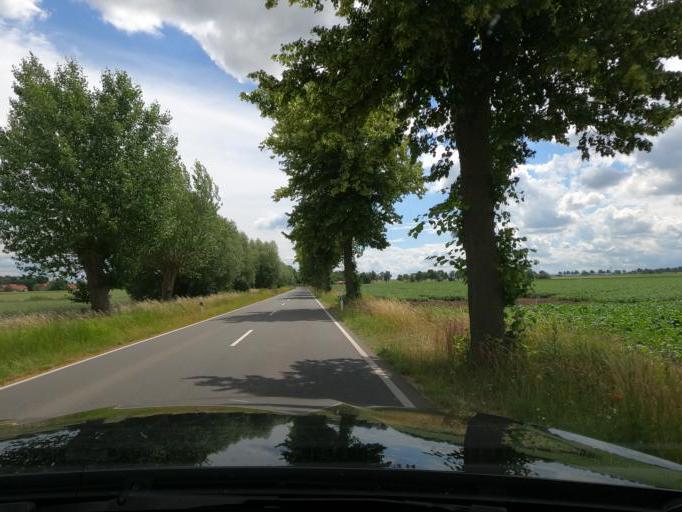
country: DE
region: Lower Saxony
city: Hohenhameln
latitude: 52.2553
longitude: 10.0181
